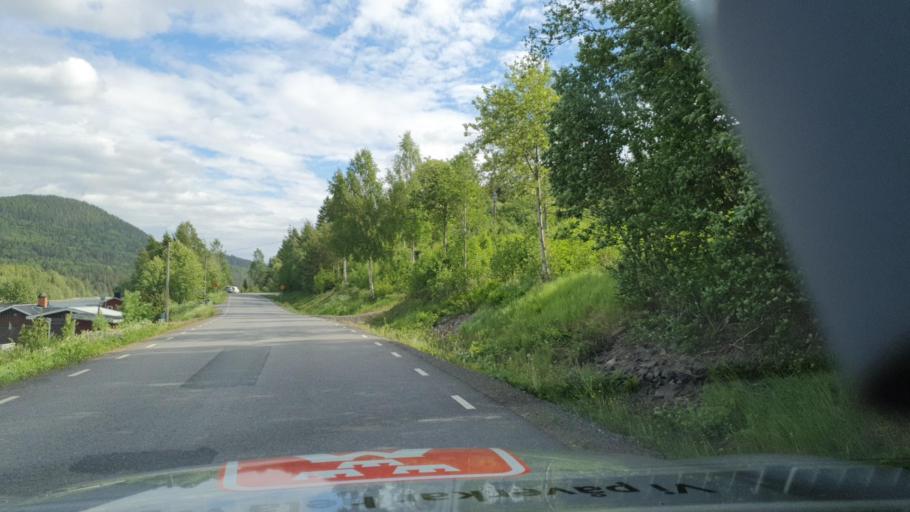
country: SE
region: Vaesternorrland
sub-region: Kramfors Kommun
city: Nordingra
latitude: 62.8260
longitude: 18.1768
